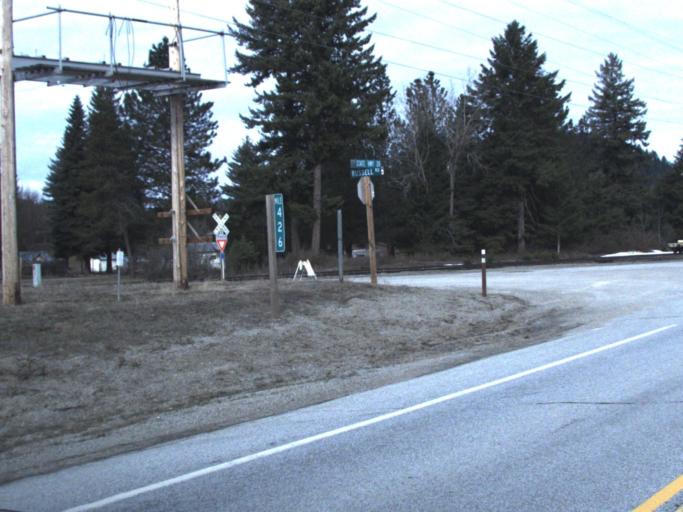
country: US
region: Washington
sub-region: Pend Oreille County
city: Newport
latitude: 48.2472
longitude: -117.2384
